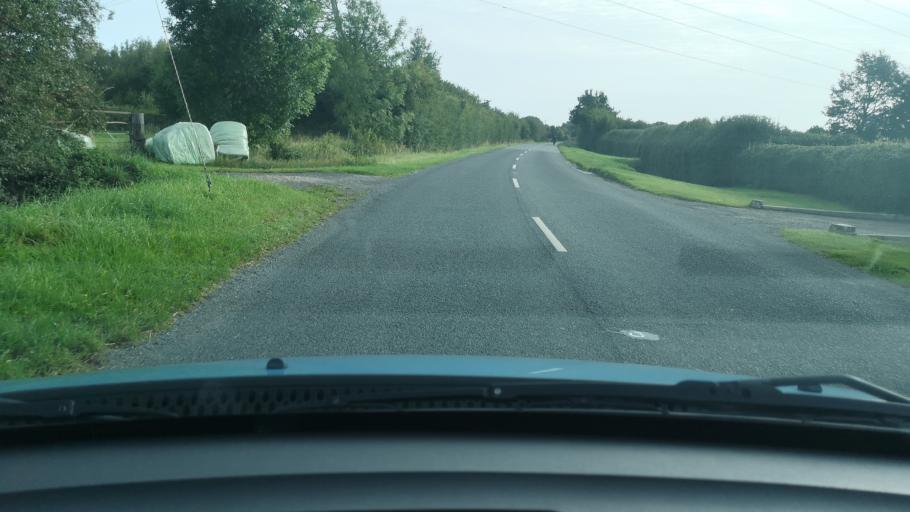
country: GB
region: England
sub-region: Doncaster
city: Fenwick
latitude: 53.6360
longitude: -1.0700
